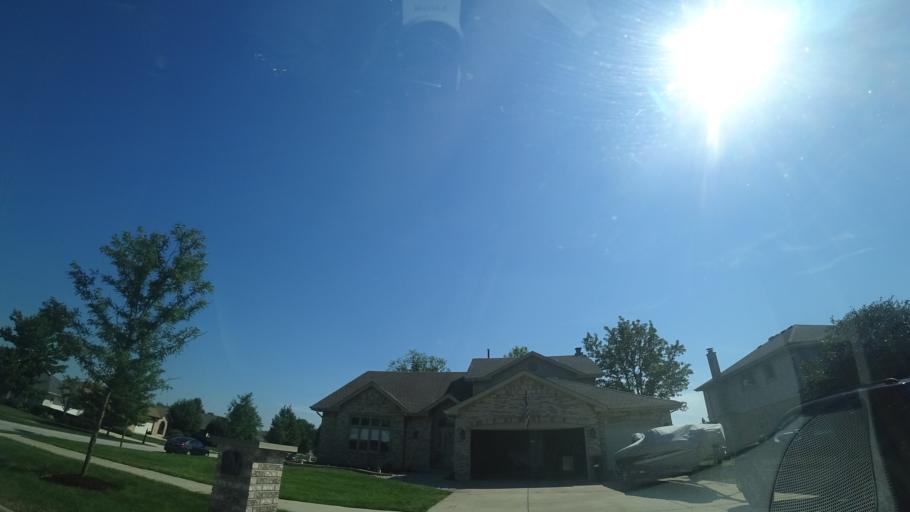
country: US
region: Illinois
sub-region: Will County
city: Homer Glen
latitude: 41.5729
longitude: -87.9074
